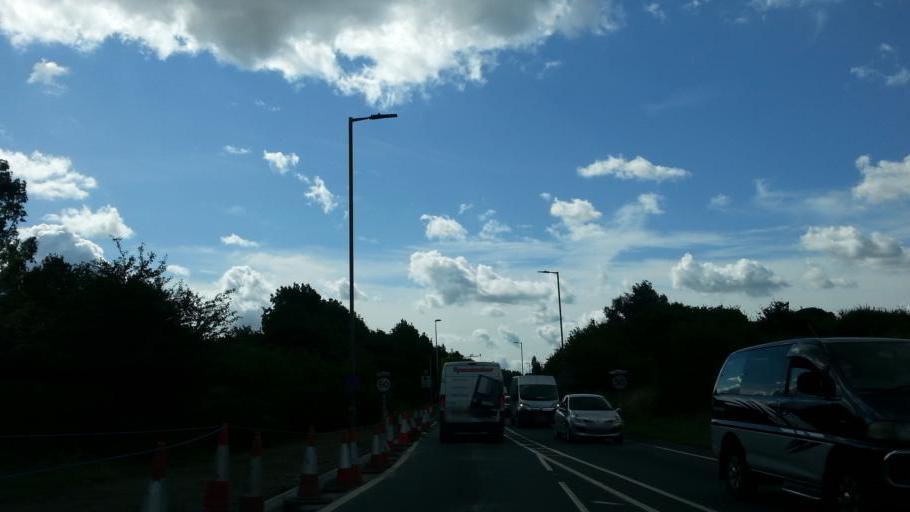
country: GB
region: England
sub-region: Essex
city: South Benfleet
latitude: 51.5650
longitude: 0.5421
